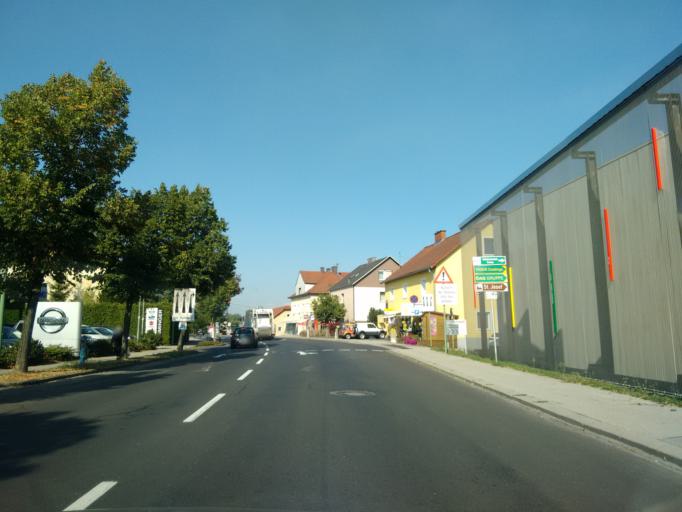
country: AT
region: Upper Austria
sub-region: Wels Stadt
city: Wels
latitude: 48.1702
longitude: 14.0513
